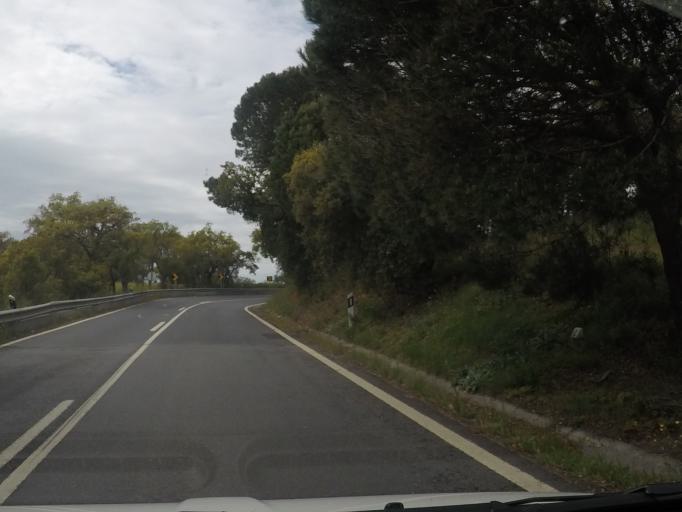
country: PT
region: Setubal
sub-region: Sines
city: Porto Covo
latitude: 37.8705
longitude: -8.7434
